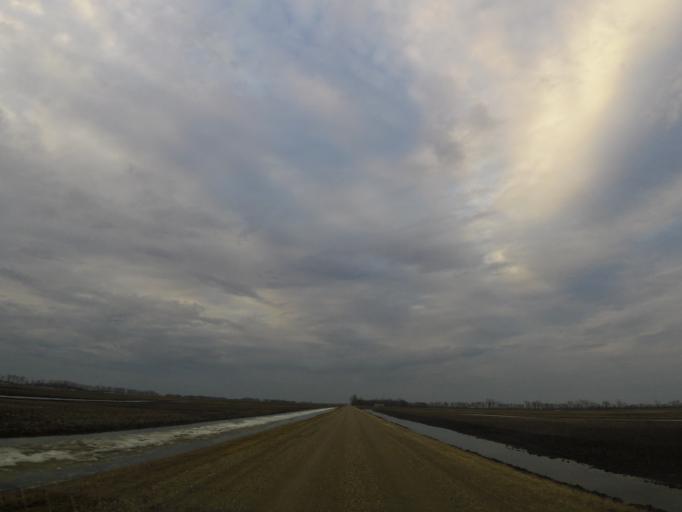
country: US
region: North Dakota
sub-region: Walsh County
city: Grafton
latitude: 48.3786
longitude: -97.2118
